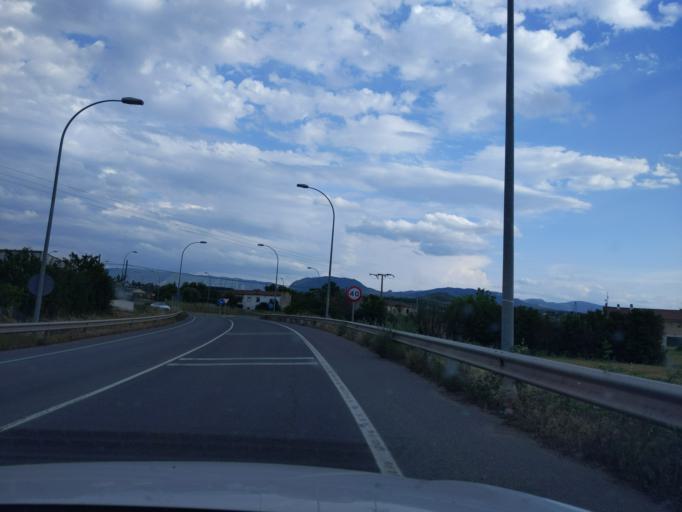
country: ES
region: La Rioja
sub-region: Provincia de La Rioja
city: Villamediana de Iregua
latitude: 42.4244
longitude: -2.4248
